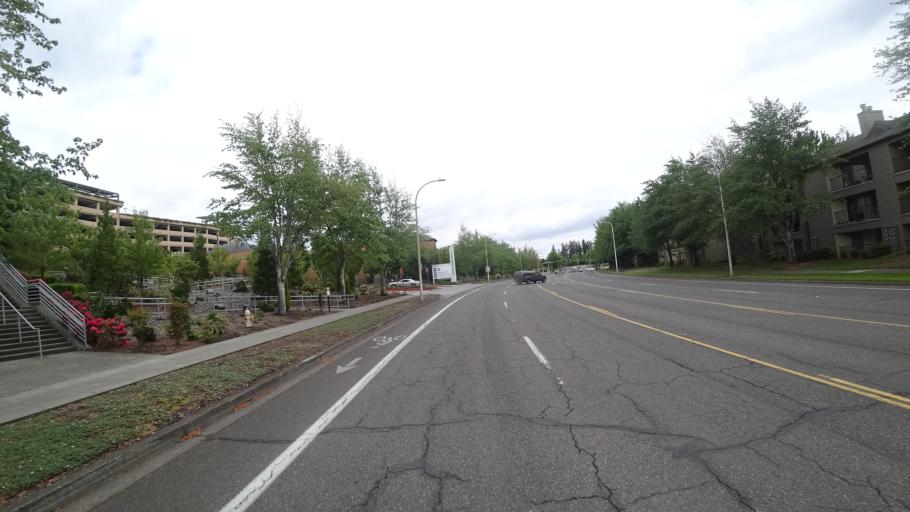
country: US
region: Oregon
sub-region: Washington County
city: Rockcreek
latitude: 45.5394
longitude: -122.8761
